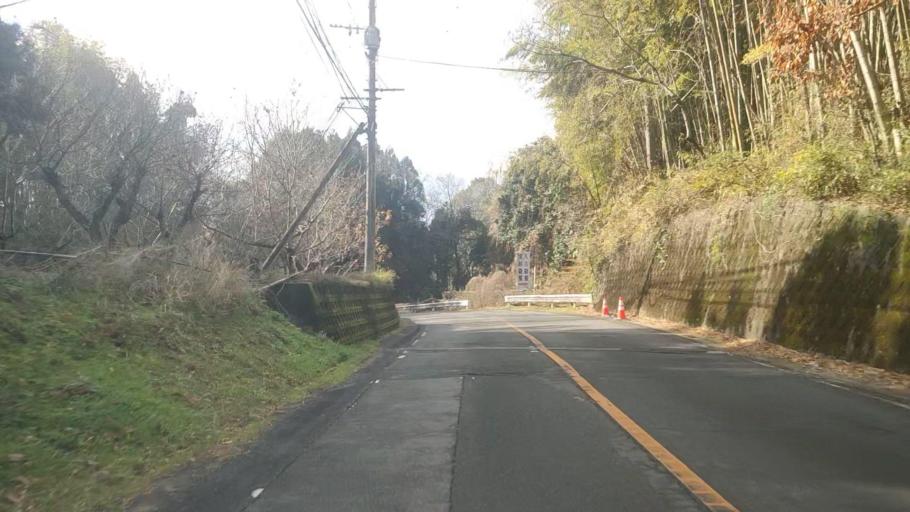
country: JP
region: Kumamoto
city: Hitoyoshi
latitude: 32.2258
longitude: 130.7806
